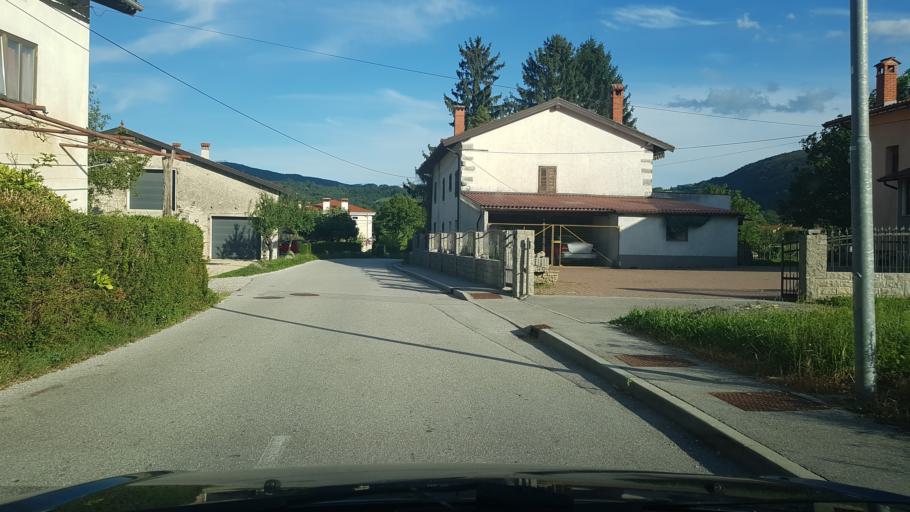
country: SI
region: Nova Gorica
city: Solkan
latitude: 45.9997
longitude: 13.6715
